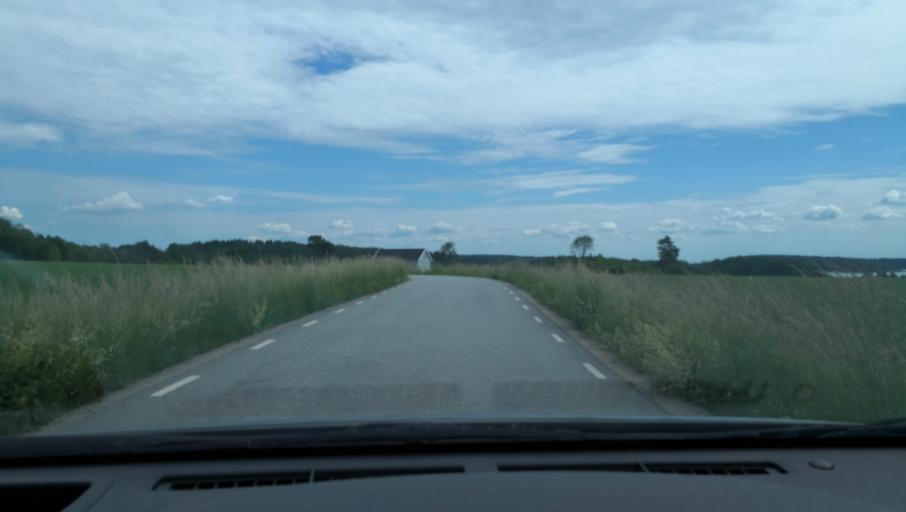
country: SE
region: Uppsala
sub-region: Habo Kommun
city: Balsta
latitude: 59.6929
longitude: 17.4722
